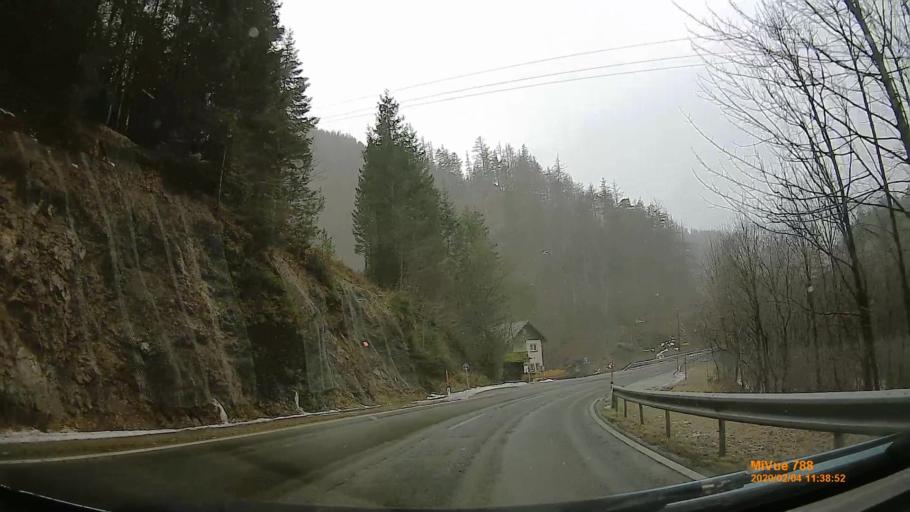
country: AT
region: Styria
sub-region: Politischer Bezirk Bruck-Muerzzuschlag
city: Neuberg an der Muerz
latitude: 47.6618
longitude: 15.5282
